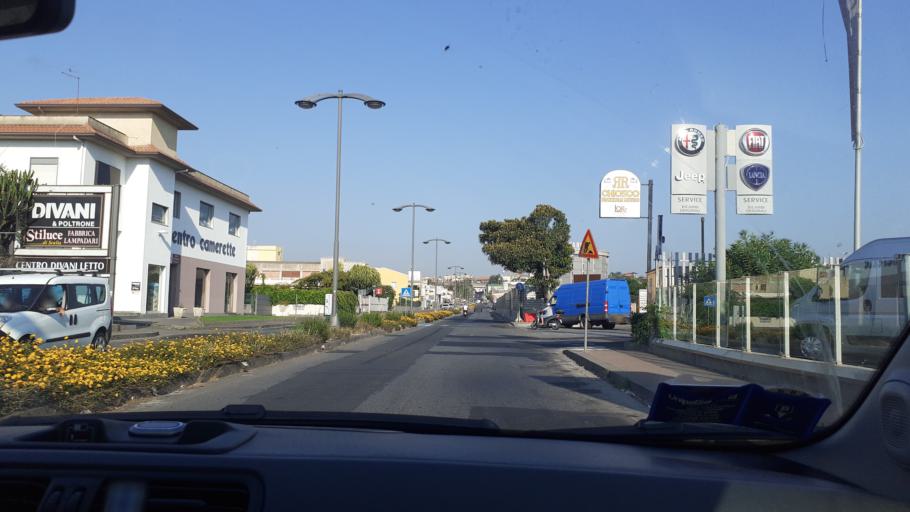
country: IT
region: Sicily
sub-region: Catania
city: Misterbianco
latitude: 37.5136
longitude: 15.0273
